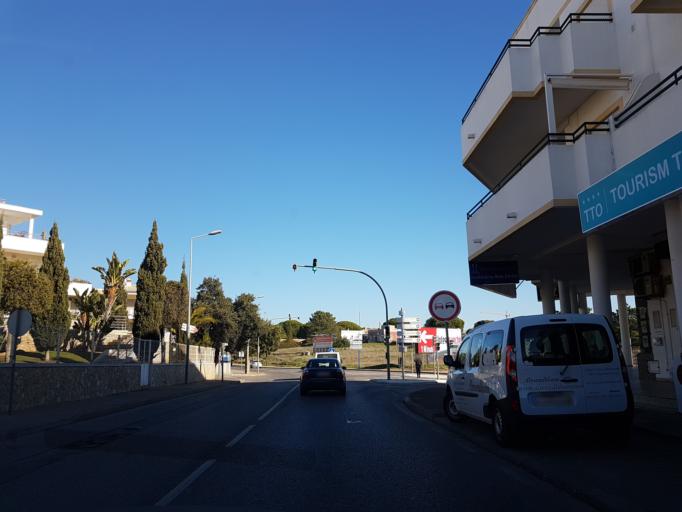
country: PT
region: Faro
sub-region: Loule
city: Boliqueime
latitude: 37.0942
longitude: -8.1883
